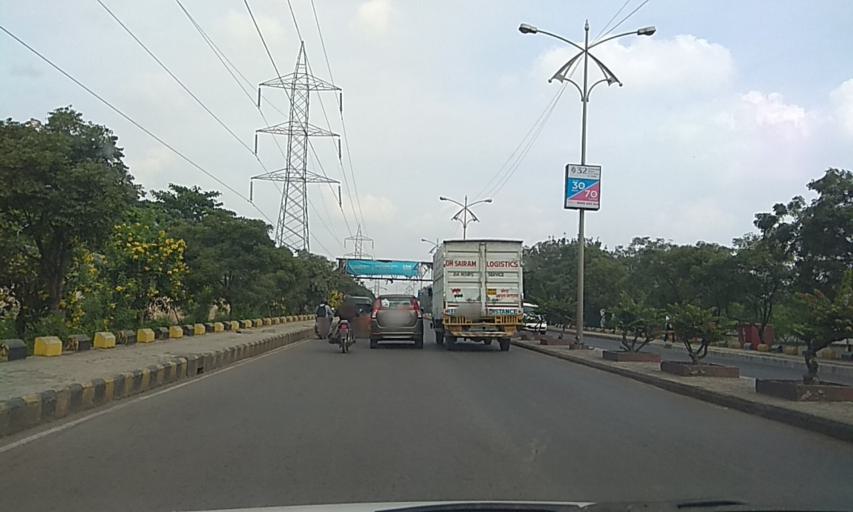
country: IN
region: Maharashtra
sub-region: Pune Division
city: Pimpri
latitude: 18.5940
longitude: 73.7088
